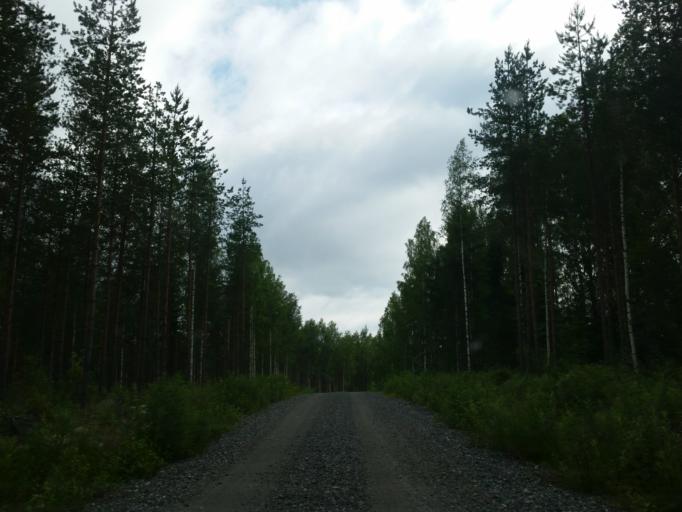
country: FI
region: Northern Savo
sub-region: Sisae-Savo
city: Tervo
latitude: 63.0554
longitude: 26.6646
